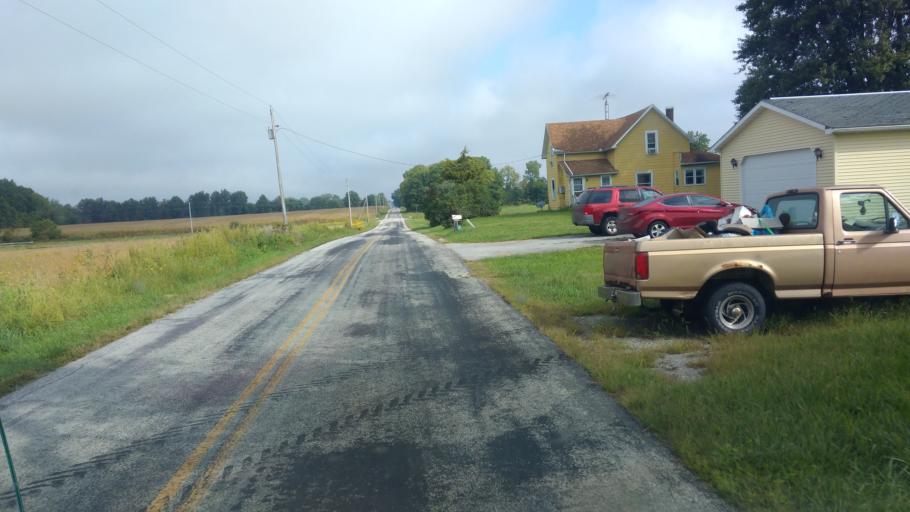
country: US
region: Ohio
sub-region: Morrow County
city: Cardington
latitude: 40.5487
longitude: -82.9767
